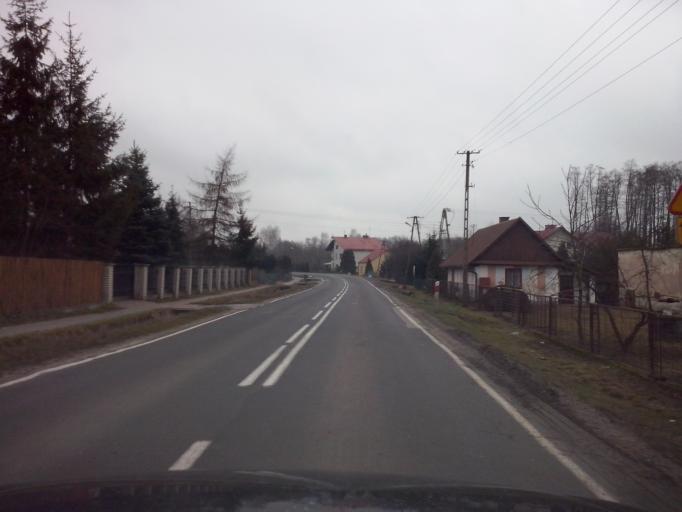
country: PL
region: Subcarpathian Voivodeship
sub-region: Powiat nizanski
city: Zarzecze
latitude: 50.5194
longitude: 22.2104
